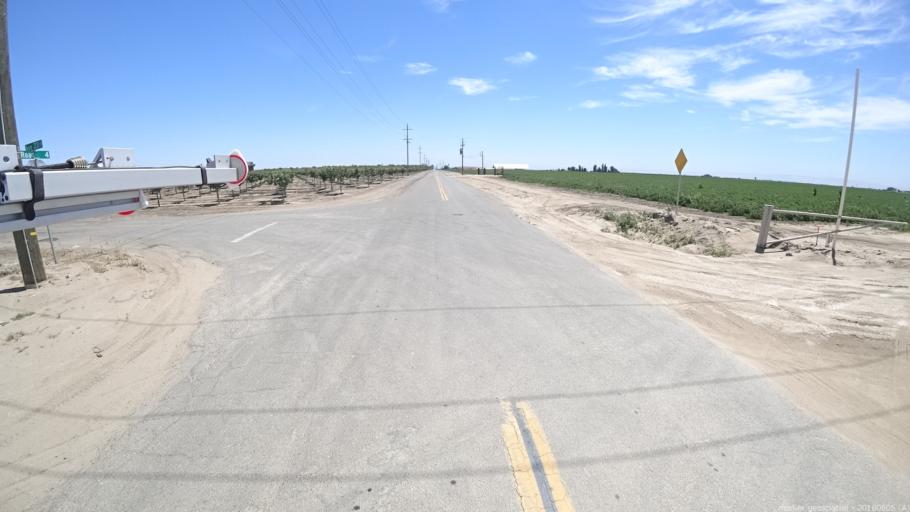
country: US
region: California
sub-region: Merced County
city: Dos Palos
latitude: 37.0908
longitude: -120.4735
